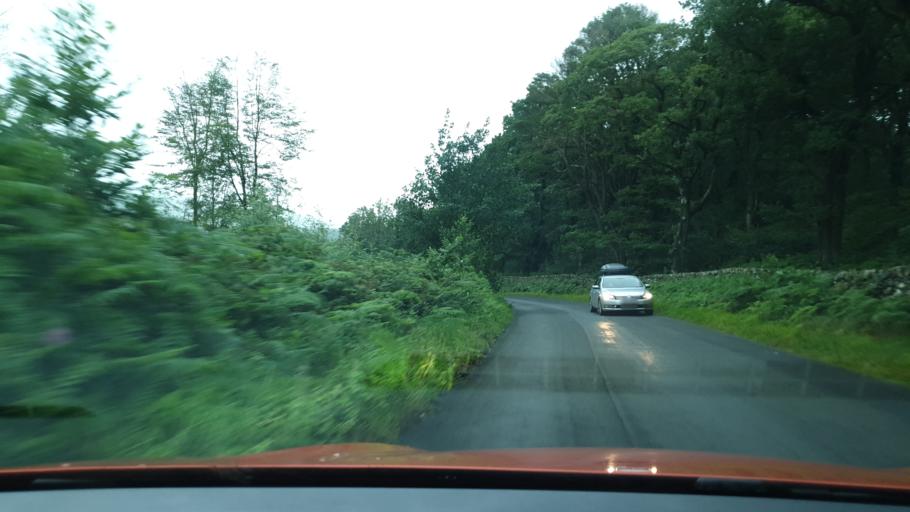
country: GB
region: England
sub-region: Cumbria
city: Seascale
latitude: 54.4110
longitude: -3.3645
